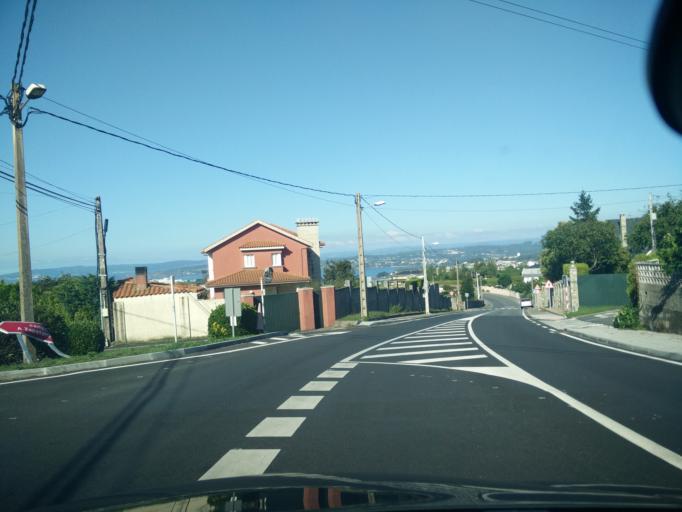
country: ES
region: Galicia
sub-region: Provincia da Coruna
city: Culleredo
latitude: 43.3251
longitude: -8.4060
